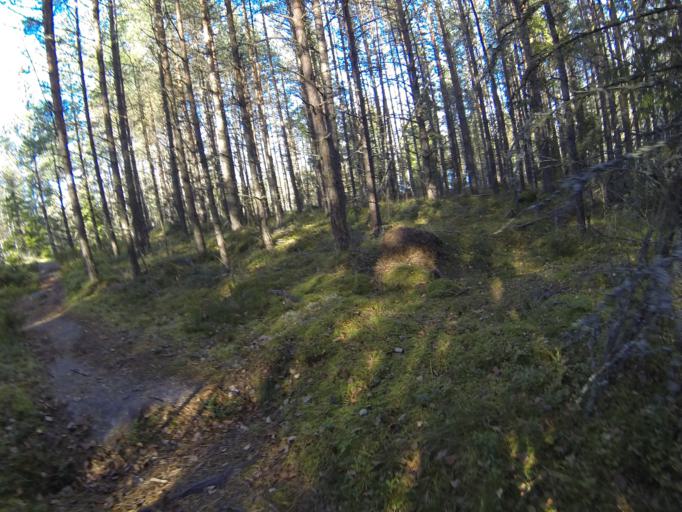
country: FI
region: Varsinais-Suomi
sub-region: Salo
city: Saerkisalo
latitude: 60.2164
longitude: 22.9655
